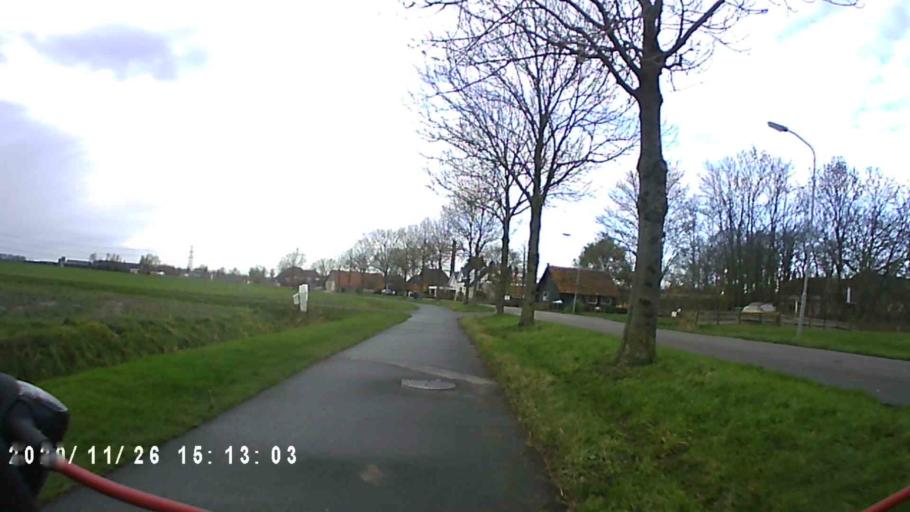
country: NL
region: Groningen
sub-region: Gemeente Appingedam
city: Appingedam
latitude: 53.3196
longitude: 6.8378
